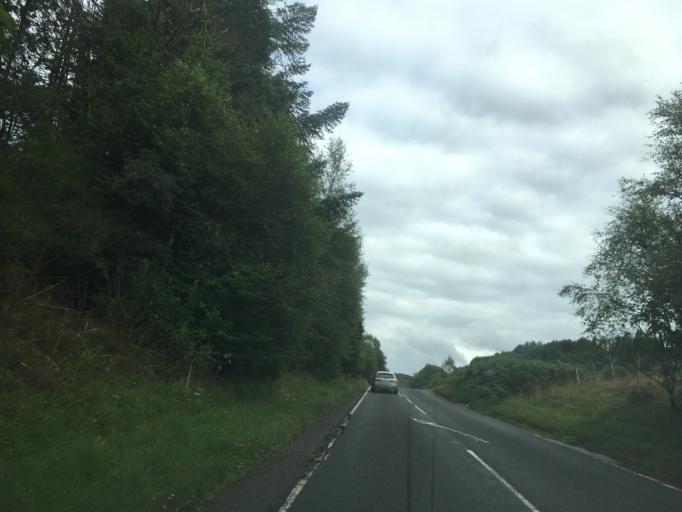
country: GB
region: Scotland
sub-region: Argyll and Bute
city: Oban
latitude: 56.3197
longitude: -5.4929
